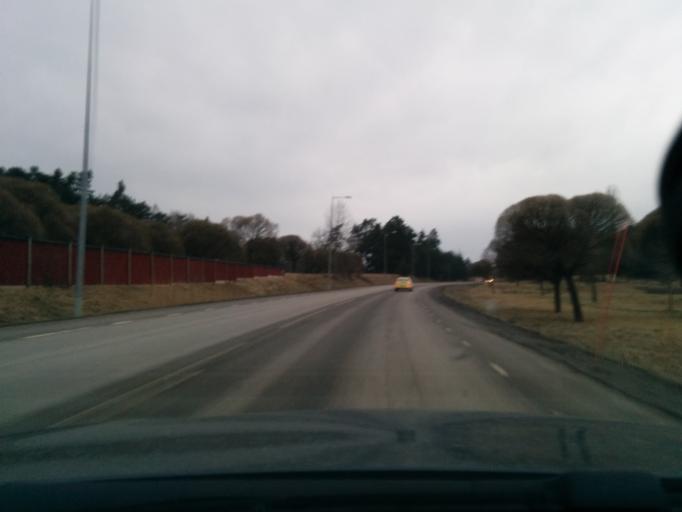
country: SE
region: Stockholm
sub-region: Taby Kommun
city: Taby
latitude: 59.4688
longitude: 18.0532
